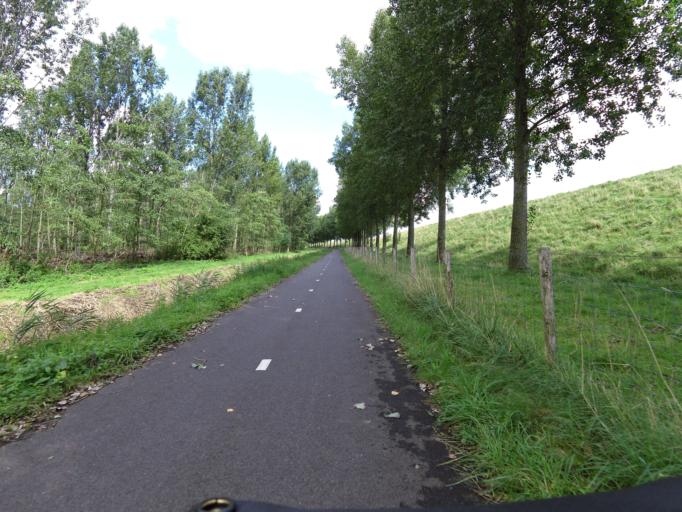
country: NL
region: North Brabant
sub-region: Gemeente Steenbergen
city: Dinteloord
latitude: 51.6747
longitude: 4.3599
